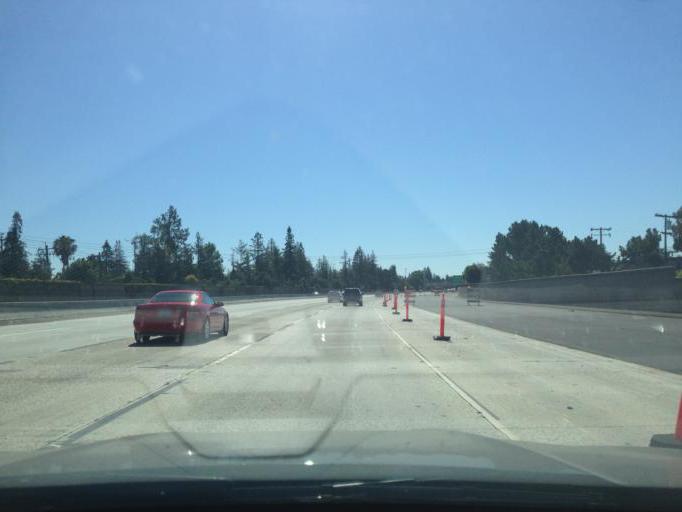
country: US
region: California
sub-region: Santa Clara County
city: Cupertino
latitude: 37.3338
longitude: -122.0216
